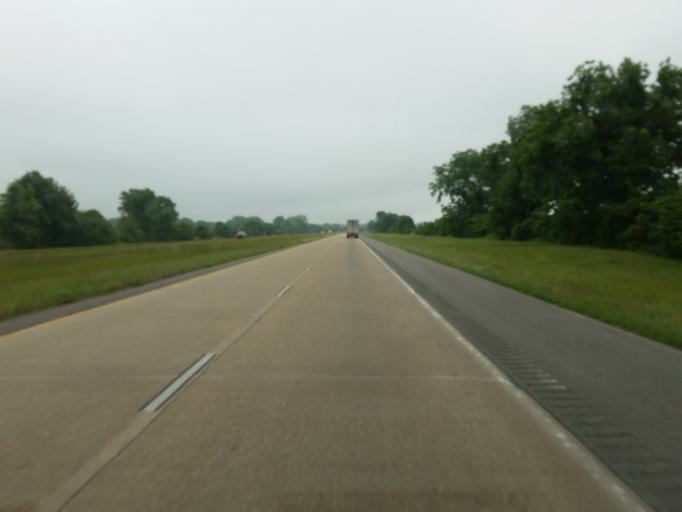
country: US
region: Louisiana
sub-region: Madison Parish
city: Tallulah
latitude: 32.3663
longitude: -91.1278
